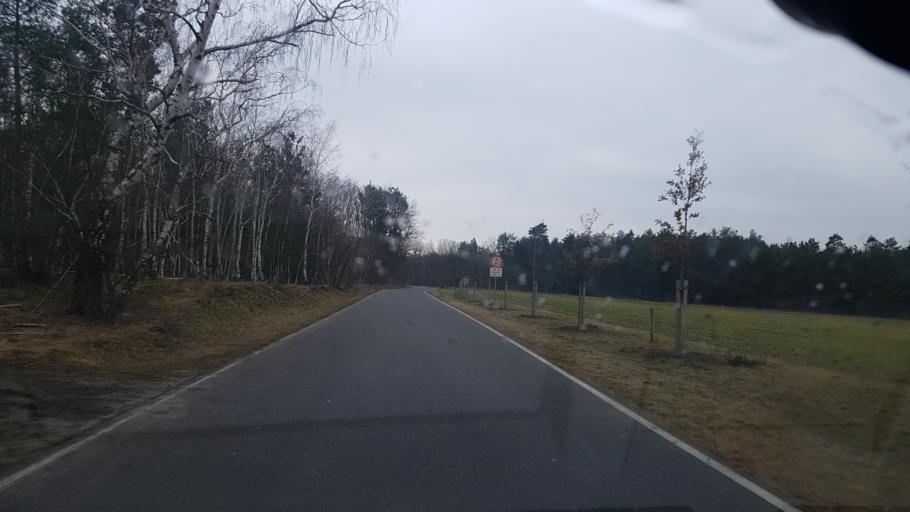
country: DE
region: Brandenburg
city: Cottbus
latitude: 51.7556
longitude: 14.4111
